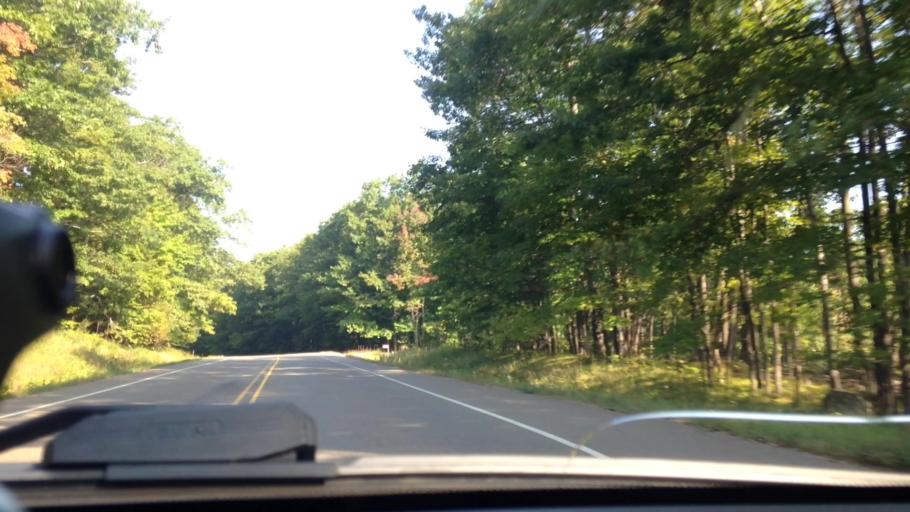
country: US
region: Michigan
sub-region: Dickinson County
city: Quinnesec
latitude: 45.8208
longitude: -87.9889
